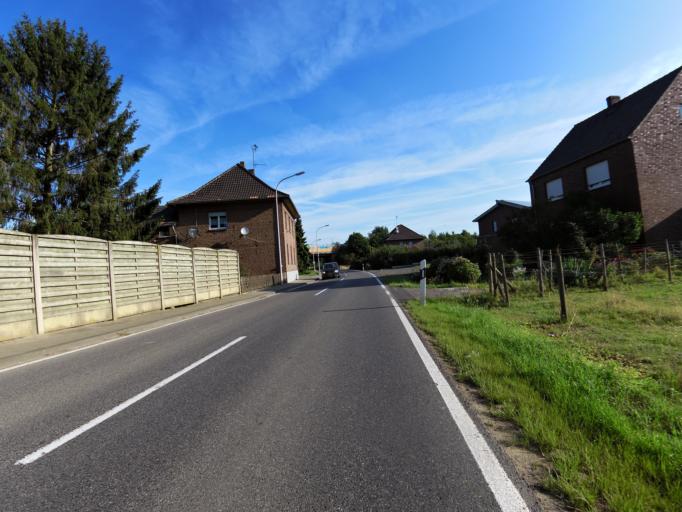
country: DE
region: North Rhine-Westphalia
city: Huckelhoven
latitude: 51.0482
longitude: 6.1744
